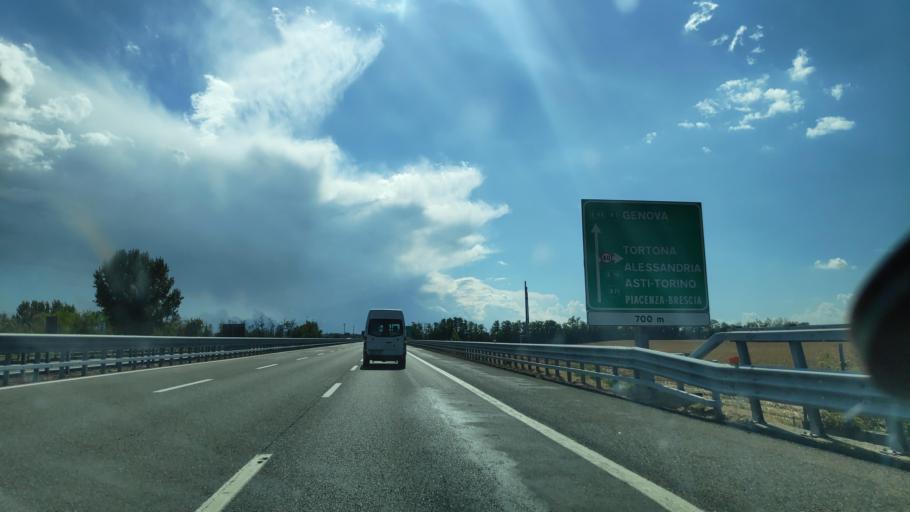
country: IT
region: Piedmont
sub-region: Provincia di Alessandria
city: Tortona
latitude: 44.9287
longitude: 8.8490
